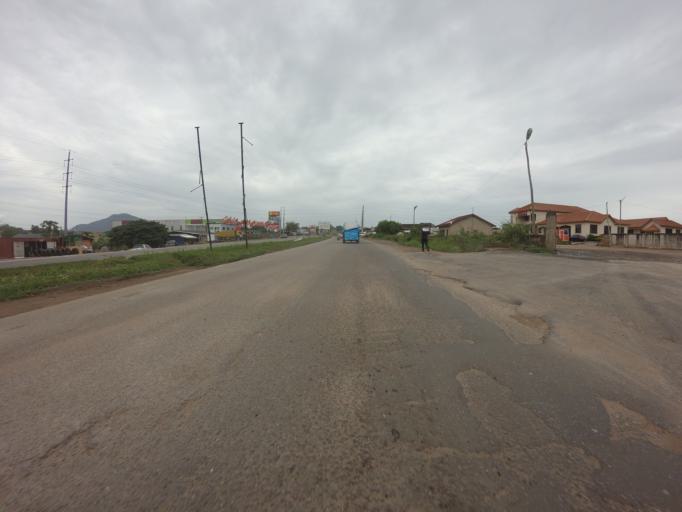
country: GH
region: Eastern
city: Nsawam
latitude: 5.7896
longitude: -0.3378
